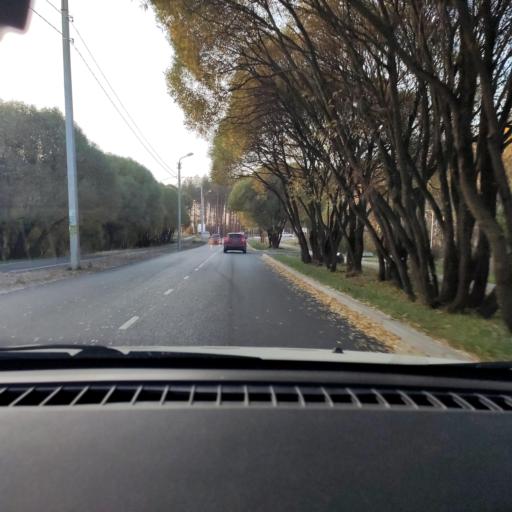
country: RU
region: Perm
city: Novyye Lyady
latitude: 58.0487
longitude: 56.5785
